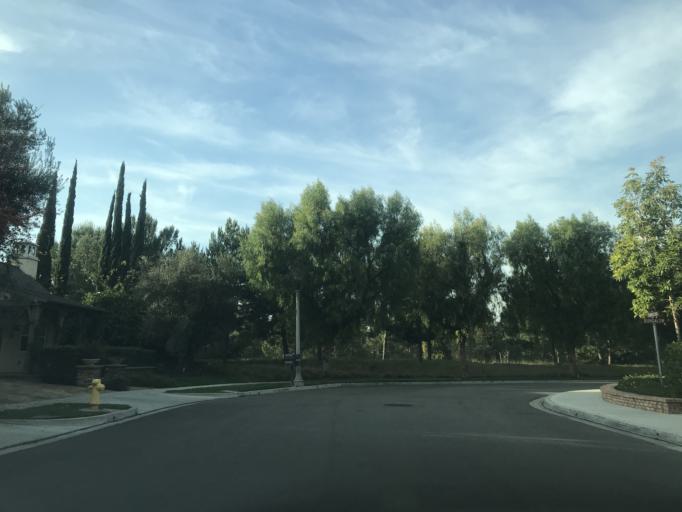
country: US
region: California
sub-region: Orange County
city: North Tustin
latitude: 33.7043
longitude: -117.7516
